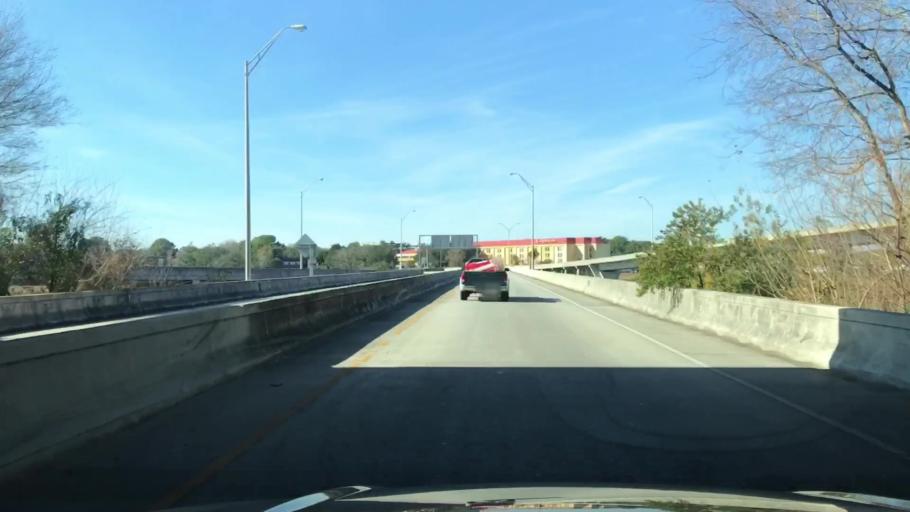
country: US
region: South Carolina
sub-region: Charleston County
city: Charleston
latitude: 32.7759
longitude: -79.9583
